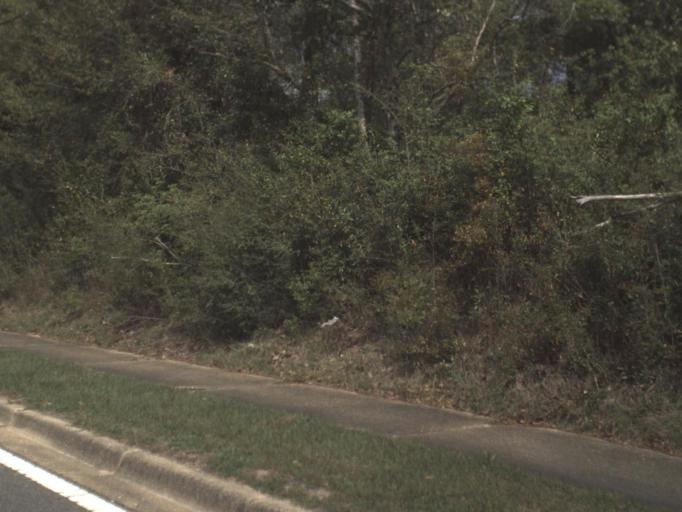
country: US
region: Florida
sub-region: Okaloosa County
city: Crestview
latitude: 30.7626
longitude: -86.5621
